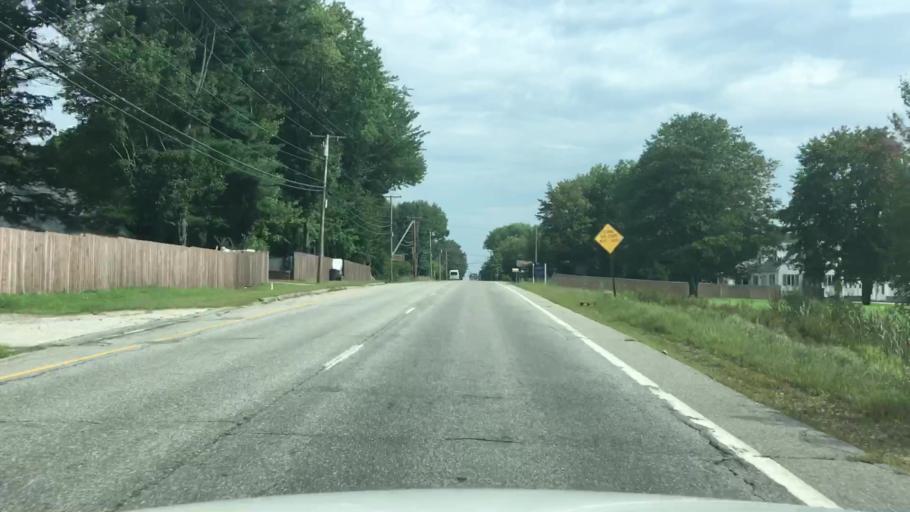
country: US
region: Maine
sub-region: Androscoggin County
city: Auburn
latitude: 44.0631
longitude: -70.2504
